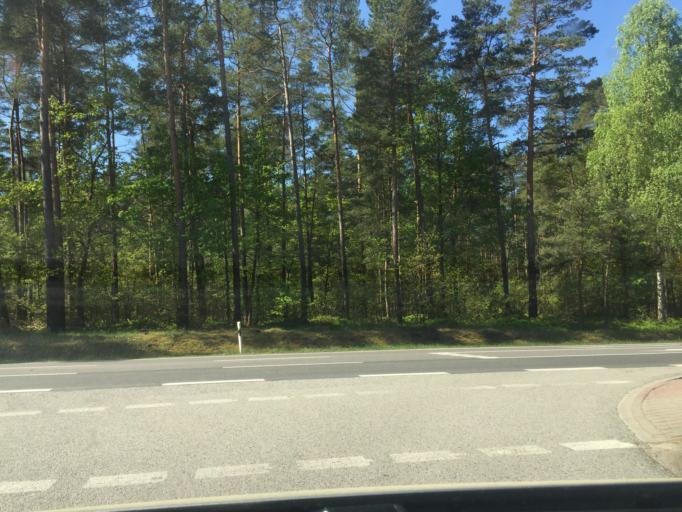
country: DE
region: Mecklenburg-Vorpommern
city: Torgelow
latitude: 53.6215
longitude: 14.0266
